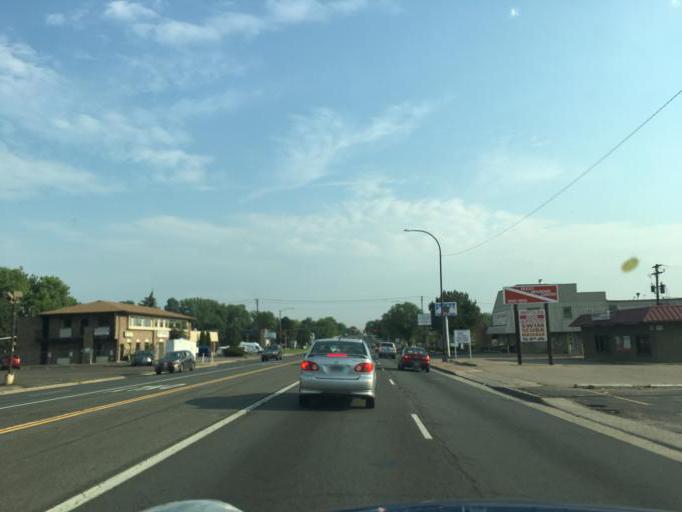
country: US
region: Colorado
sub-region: Jefferson County
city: Edgewater
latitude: 39.7459
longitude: -105.0814
